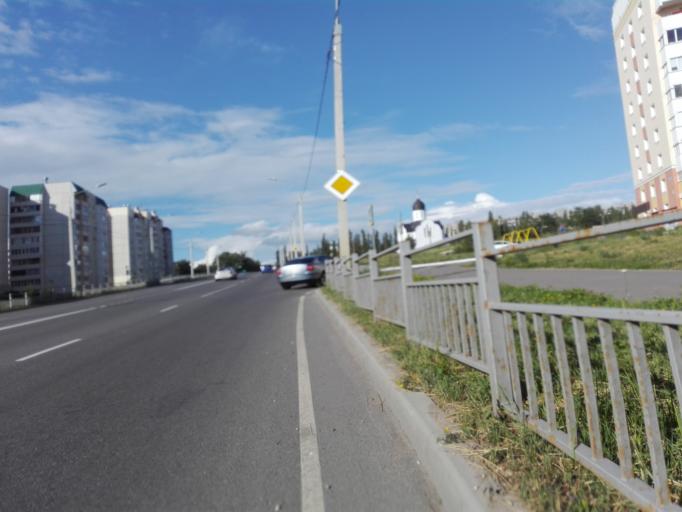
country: RU
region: Orjol
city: Orel
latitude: 53.0150
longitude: 36.1329
